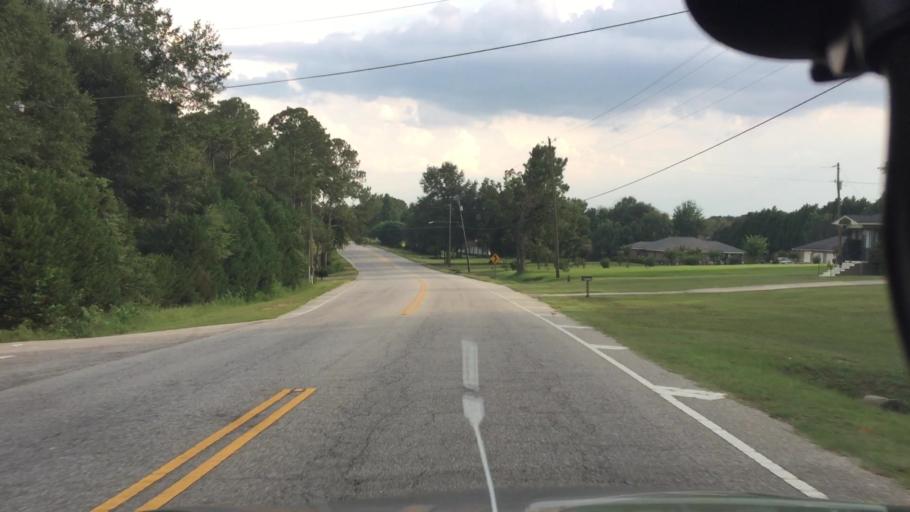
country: US
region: Alabama
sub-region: Coffee County
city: Enterprise
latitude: 31.3611
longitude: -85.8316
